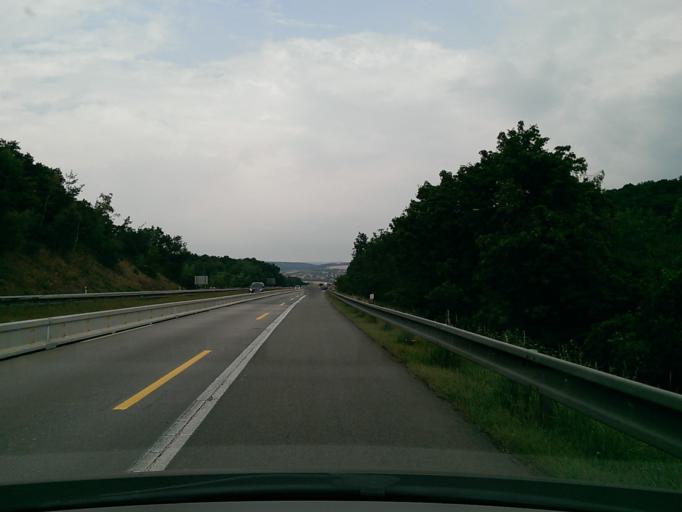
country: CZ
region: South Moravian
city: Ricany
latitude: 49.1950
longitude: 16.4314
